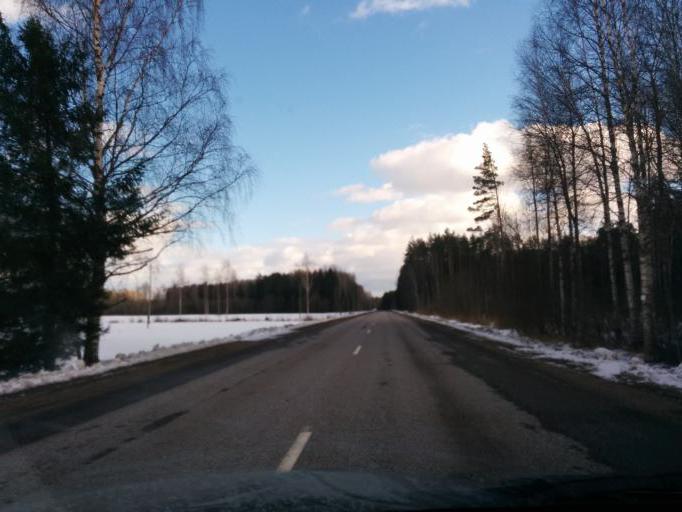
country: LV
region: Rugaju
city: Rugaji
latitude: 57.1815
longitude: 27.0752
